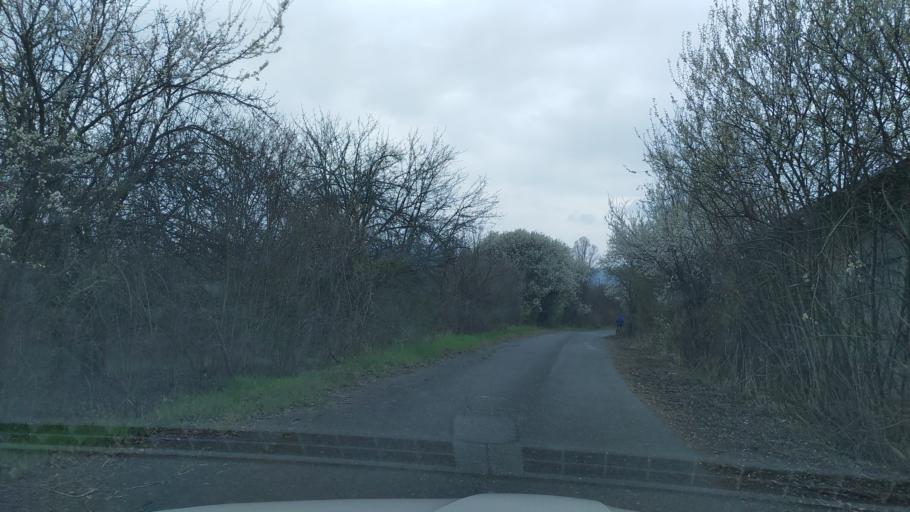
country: CZ
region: Ustecky
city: Chabarovice
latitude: 50.6620
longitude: 13.9309
